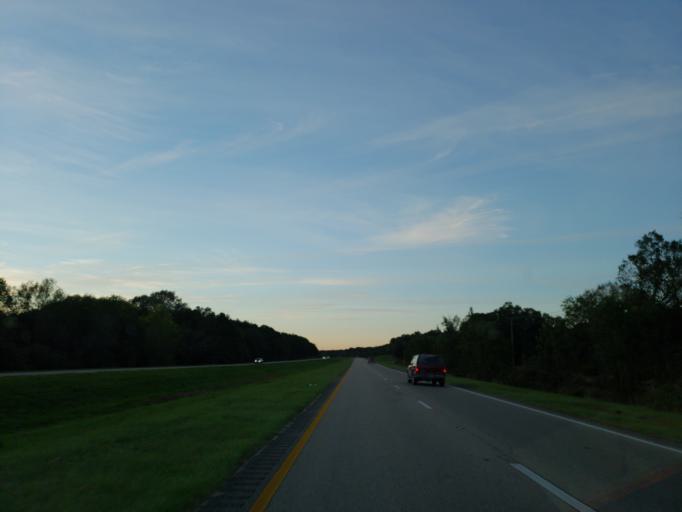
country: US
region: Mississippi
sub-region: Wayne County
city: Belmont
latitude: 31.5949
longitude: -88.5525
